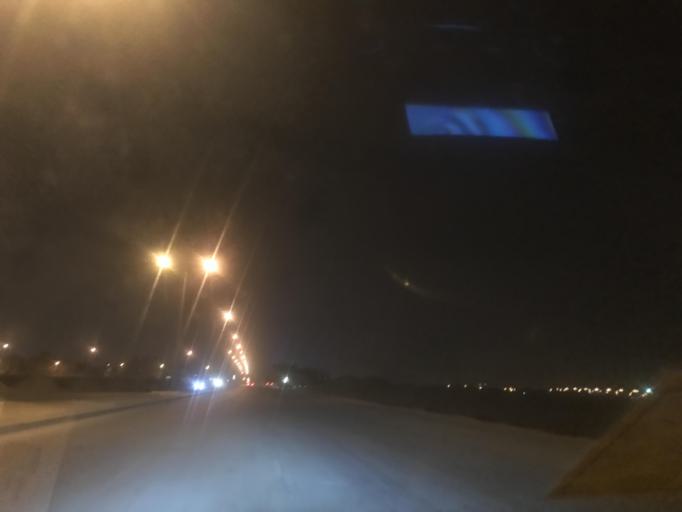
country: SA
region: Ar Riyad
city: Riyadh
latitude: 24.8128
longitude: 46.5872
